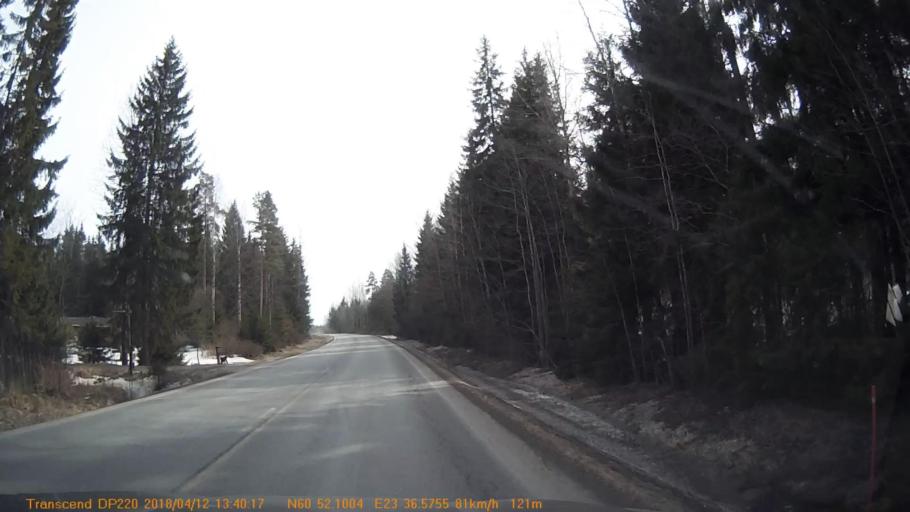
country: FI
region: Haeme
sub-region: Forssa
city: Forssa
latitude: 60.8676
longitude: 23.6101
